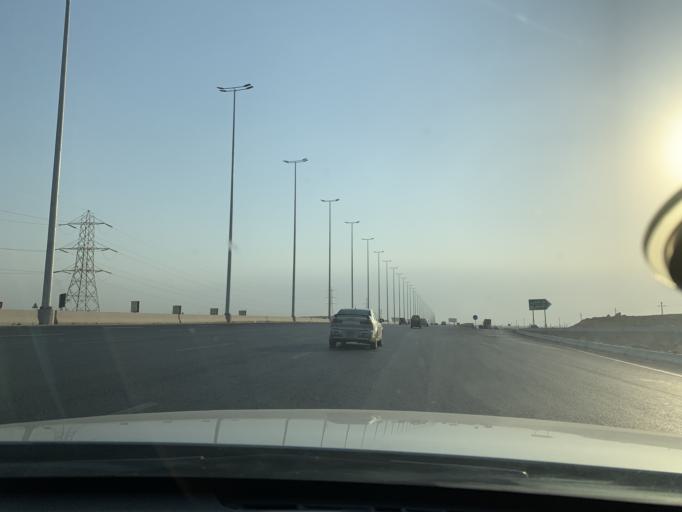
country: EG
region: Muhafazat al Qalyubiyah
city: Al Khankah
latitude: 30.1059
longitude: 31.6044
